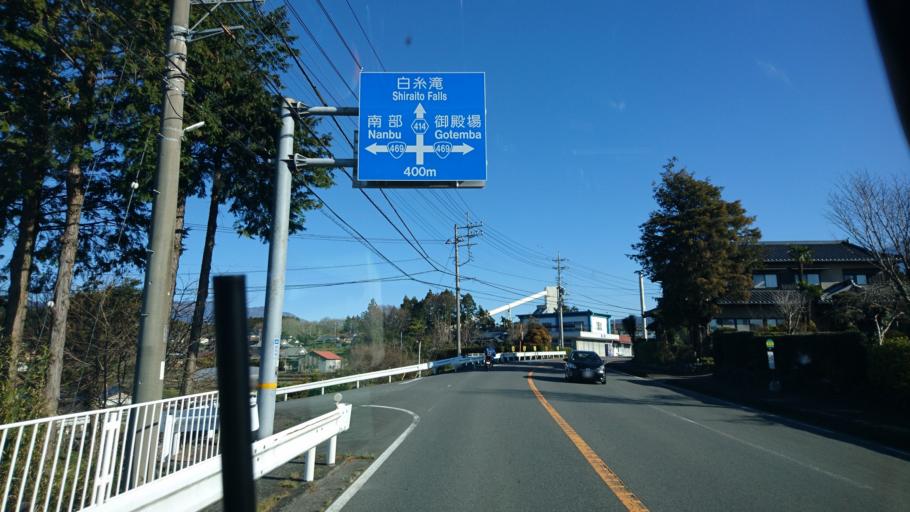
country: JP
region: Shizuoka
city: Fujinomiya
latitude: 35.2729
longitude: 138.6022
